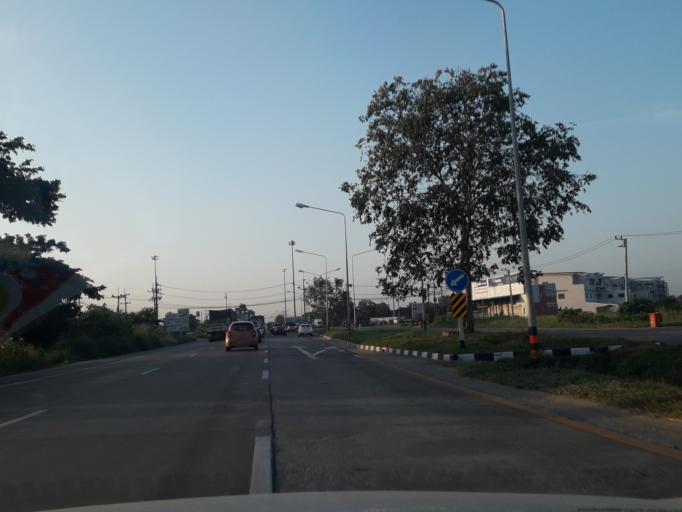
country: TH
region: Phra Nakhon Si Ayutthaya
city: Bang Ban
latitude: 14.3540
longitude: 100.5285
